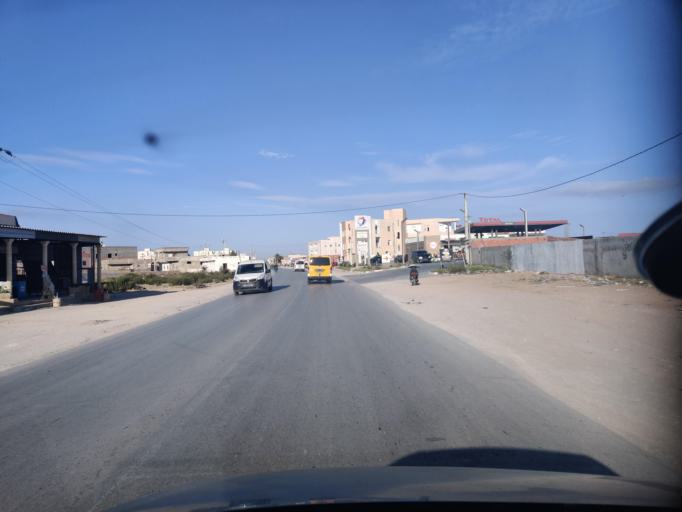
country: TN
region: Ariana
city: Ariana
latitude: 36.9561
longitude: 10.2230
